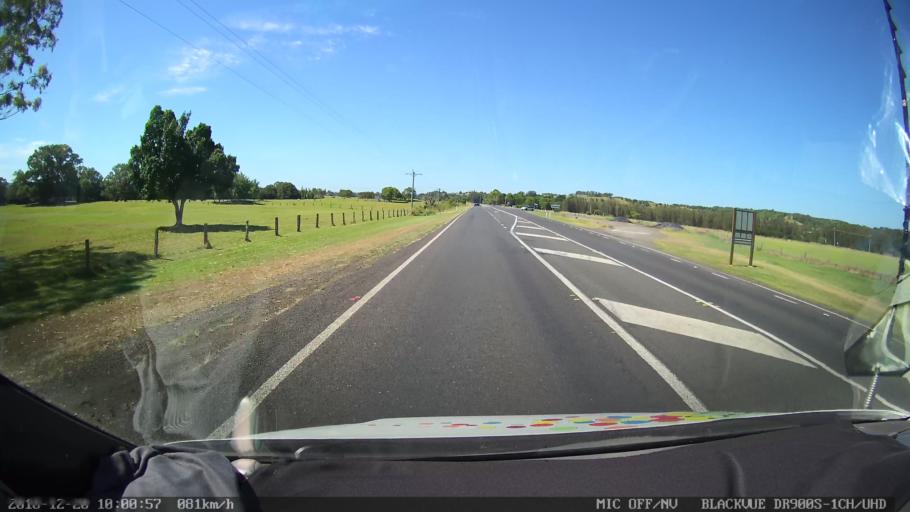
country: AU
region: New South Wales
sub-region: Lismore Municipality
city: Lismore
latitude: -28.8383
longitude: 153.2640
